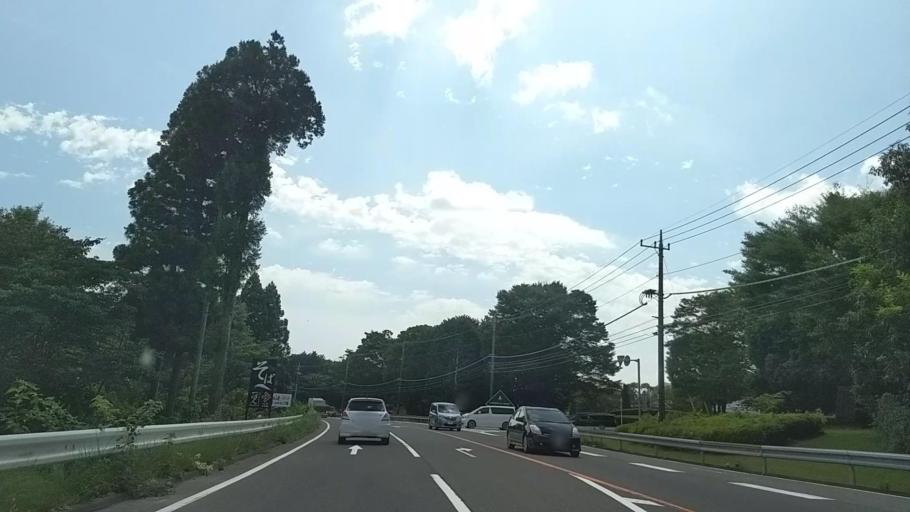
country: JP
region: Shizuoka
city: Fujinomiya
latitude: 35.3349
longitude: 138.5839
